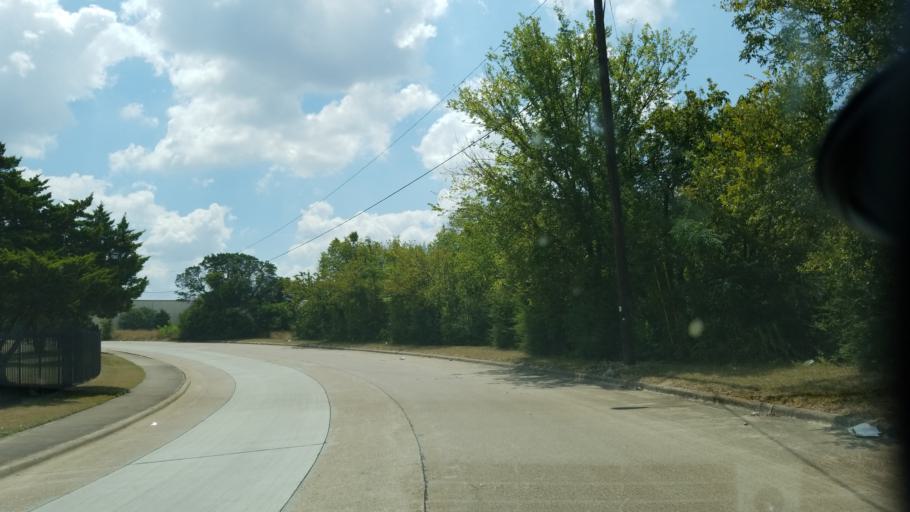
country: US
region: Texas
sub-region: Dallas County
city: Duncanville
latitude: 32.6930
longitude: -96.9004
